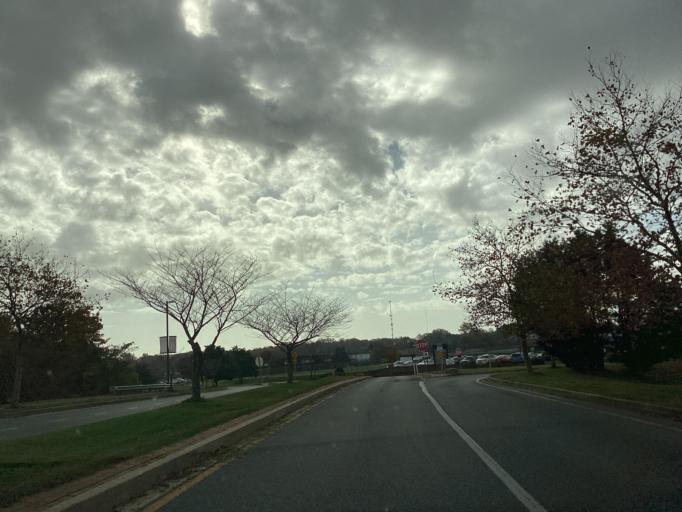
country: US
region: Maryland
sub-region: Somerset County
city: Princess Anne
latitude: 38.2137
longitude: -75.6864
